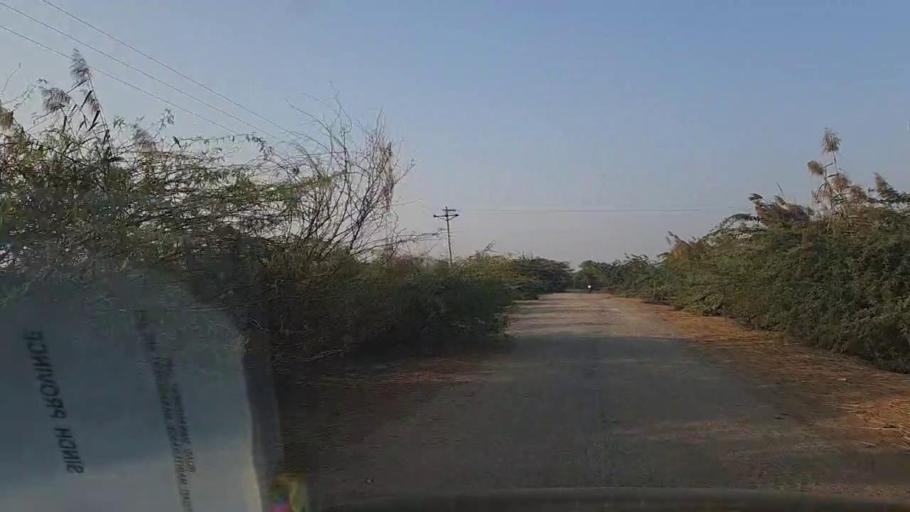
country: PK
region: Sindh
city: Keti Bandar
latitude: 24.2853
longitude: 67.5874
